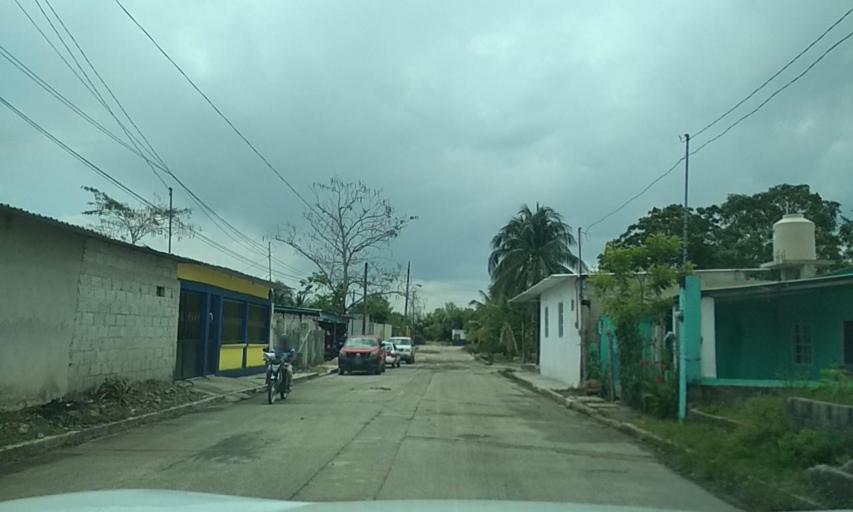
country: MX
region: Veracruz
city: Las Choapas
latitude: 17.8949
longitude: -94.0977
